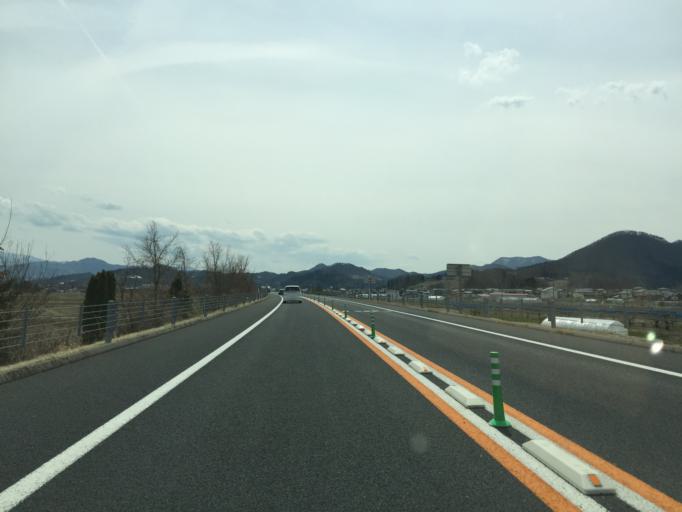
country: JP
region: Yamagata
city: Kaminoyama
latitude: 38.2370
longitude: 140.2750
